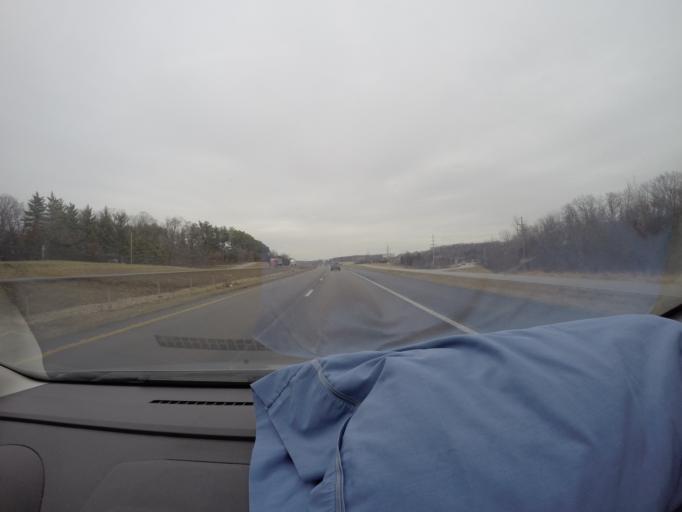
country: US
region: Missouri
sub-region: Warren County
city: Warrenton
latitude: 38.8196
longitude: -91.1721
